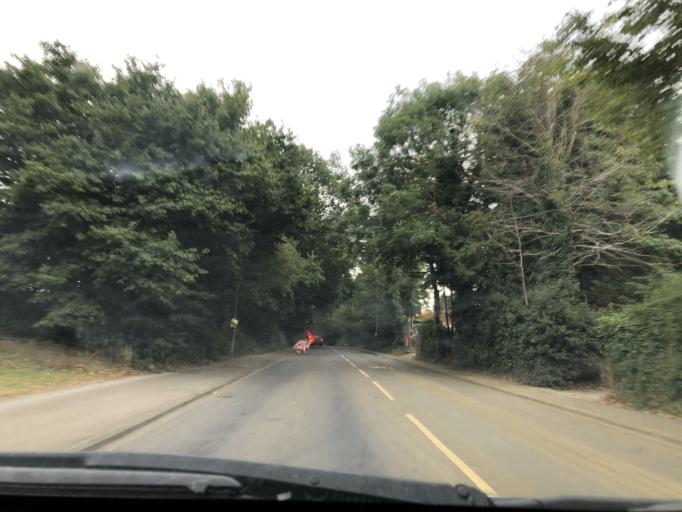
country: GB
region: England
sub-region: Kent
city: Sevenoaks
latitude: 51.2634
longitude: 0.1945
